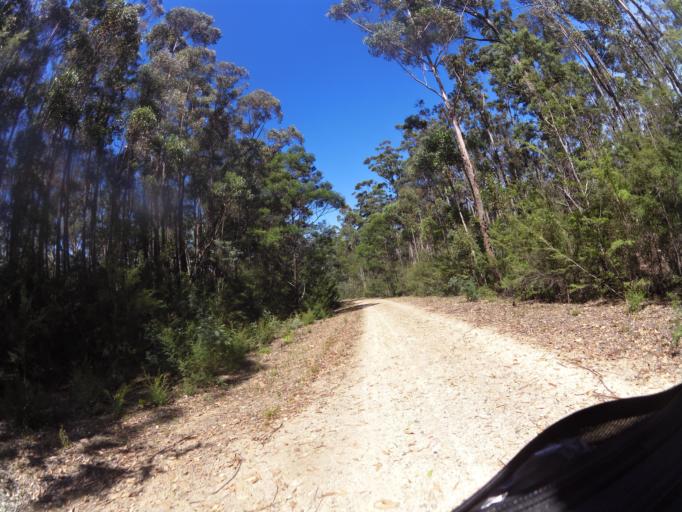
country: AU
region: Victoria
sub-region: East Gippsland
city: Lakes Entrance
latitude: -37.7231
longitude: 148.1125
